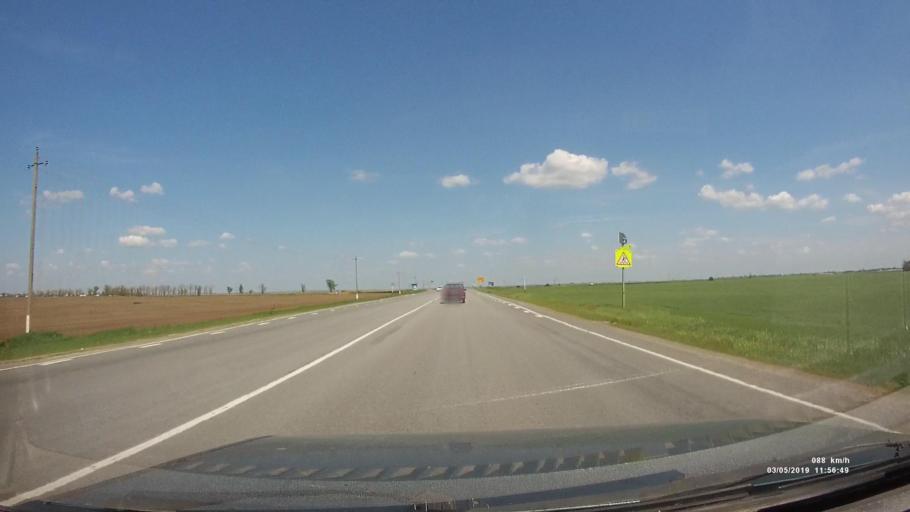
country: RU
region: Rostov
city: Bagayevskaya
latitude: 47.1993
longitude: 40.3044
